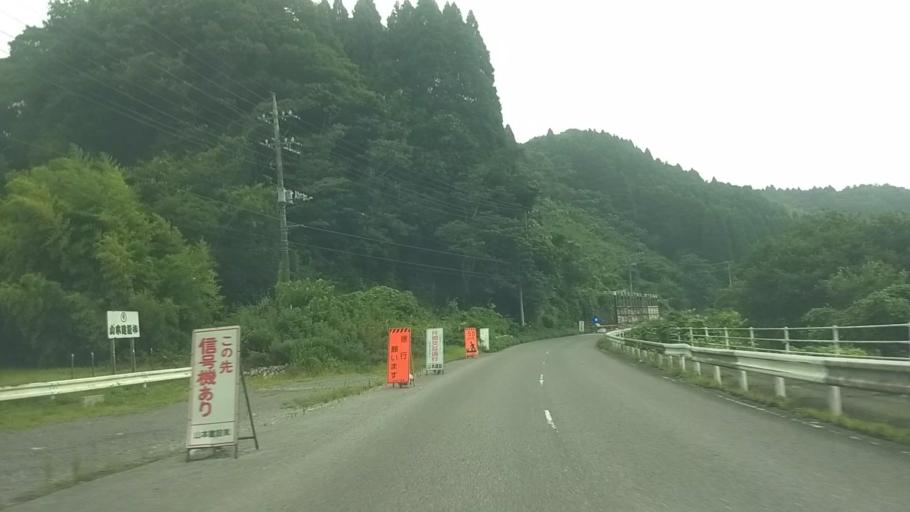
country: JP
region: Chiba
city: Katsuura
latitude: 35.2560
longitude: 140.2437
